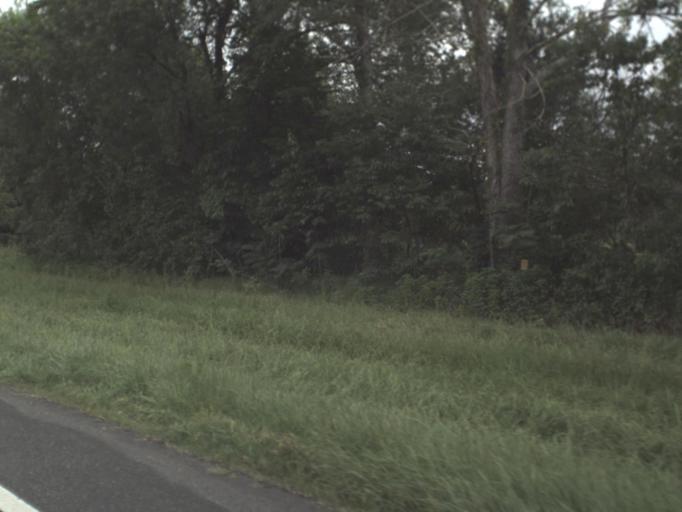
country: US
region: Florida
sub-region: Levy County
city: Williston
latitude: 29.3313
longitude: -82.4549
